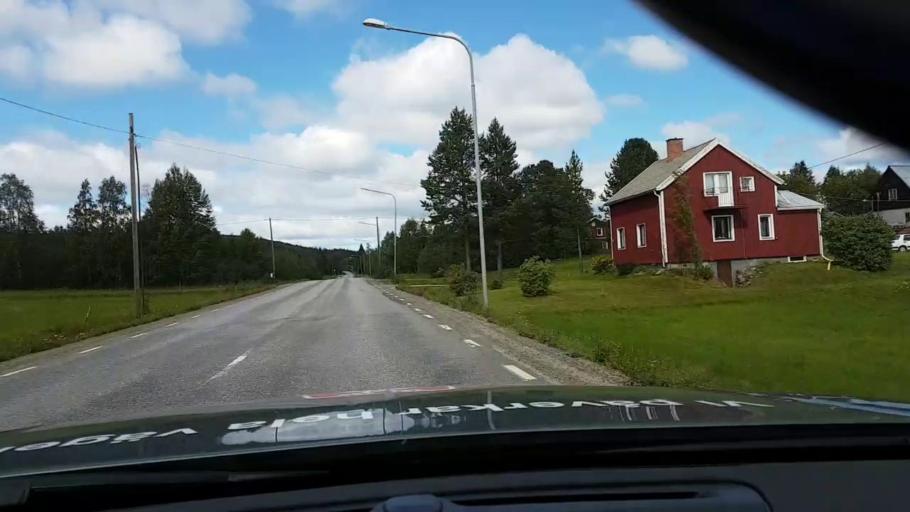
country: SE
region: Vaesternorrland
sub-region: OErnskoeldsviks Kommun
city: Bredbyn
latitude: 63.4817
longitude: 18.0903
